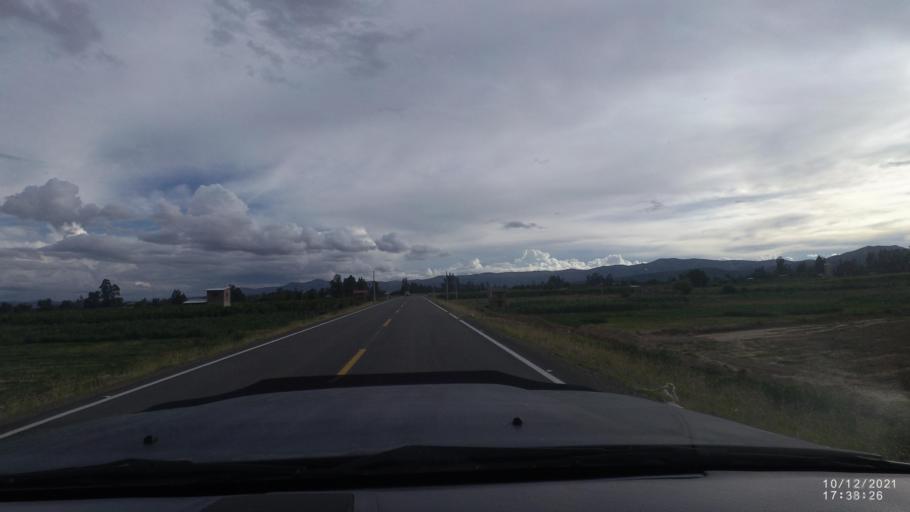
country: BO
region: Cochabamba
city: Tarata
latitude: -17.5696
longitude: -66.0095
